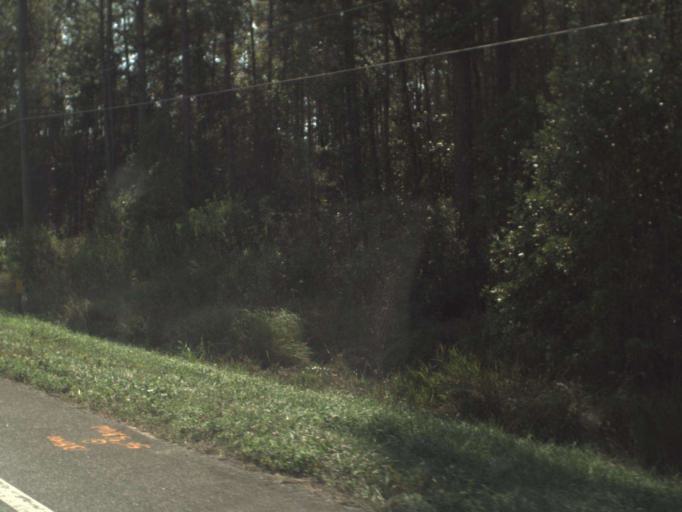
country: US
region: Florida
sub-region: Holmes County
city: Bonifay
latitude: 30.7118
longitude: -85.6859
